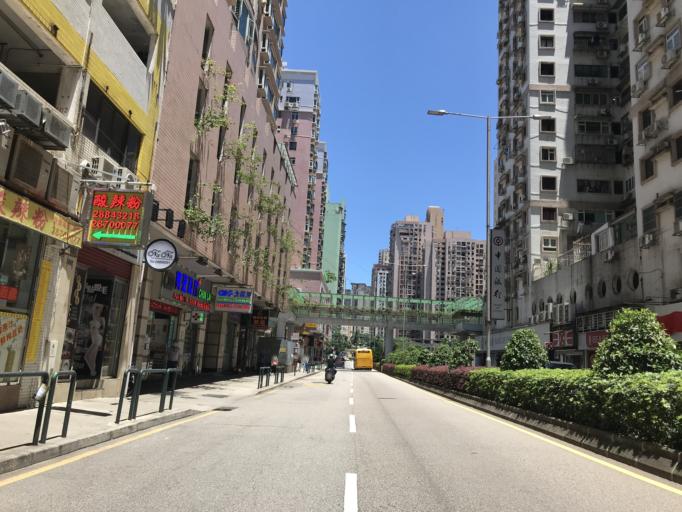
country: MO
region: Macau
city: Macau
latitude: 22.1615
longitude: 113.5560
